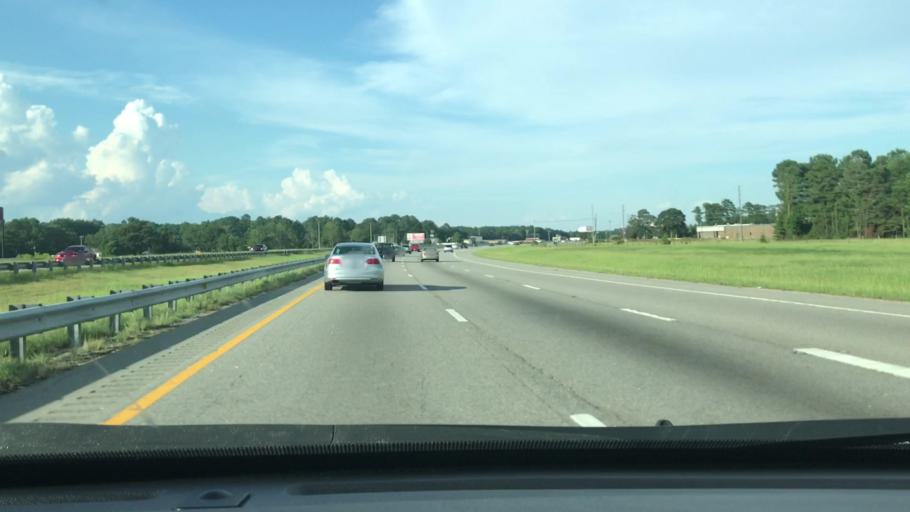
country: US
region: North Carolina
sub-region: Robeson County
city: Lumberton
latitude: 34.6015
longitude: -79.1034
